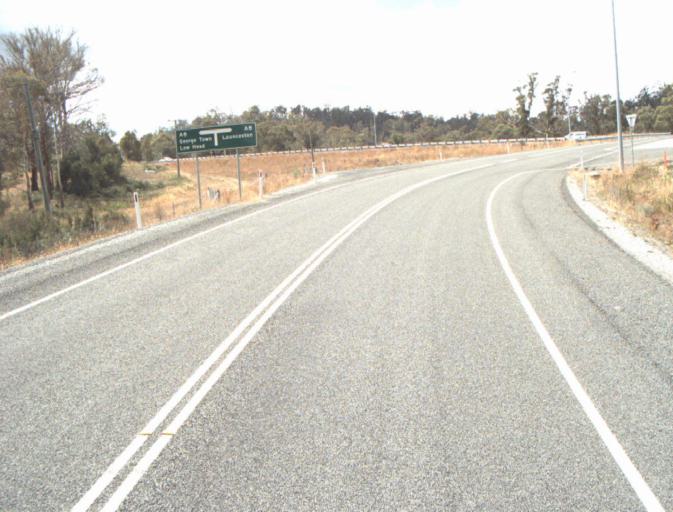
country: AU
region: Tasmania
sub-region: Launceston
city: Mayfield
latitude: -41.3030
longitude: 147.0491
